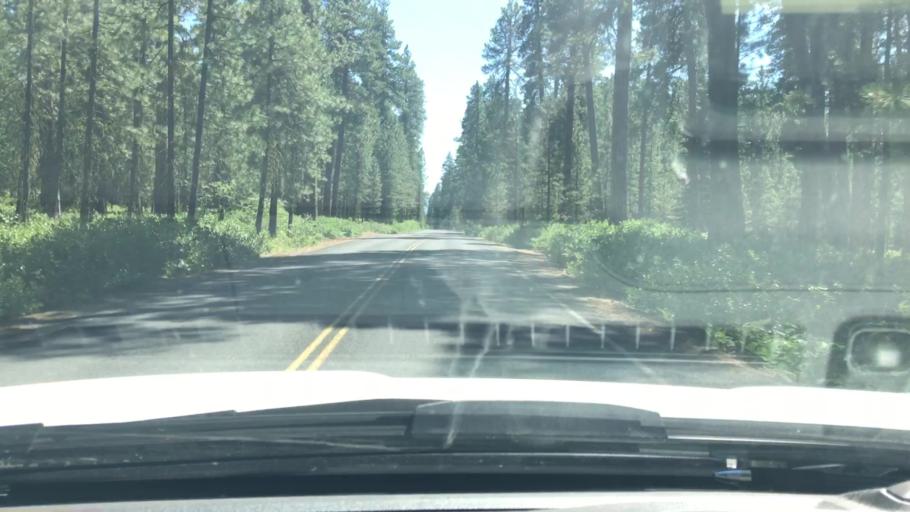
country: US
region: Oregon
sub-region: Deschutes County
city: Sisters
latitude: 44.4212
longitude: -121.6682
